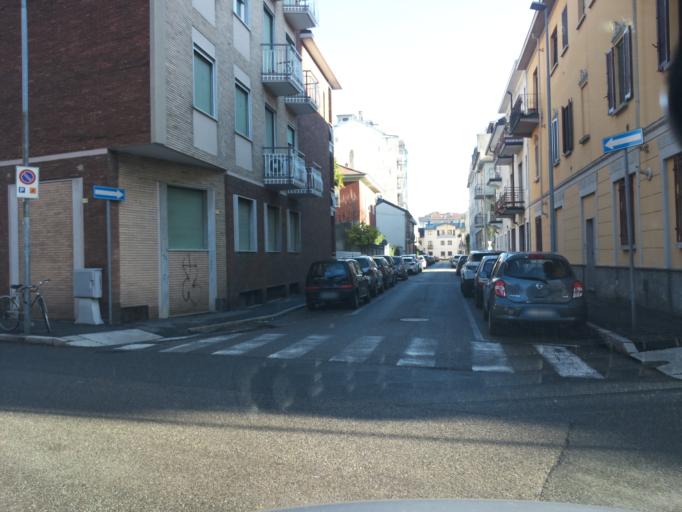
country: IT
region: Piedmont
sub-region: Provincia di Novara
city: Novara
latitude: 45.4408
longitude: 8.6114
